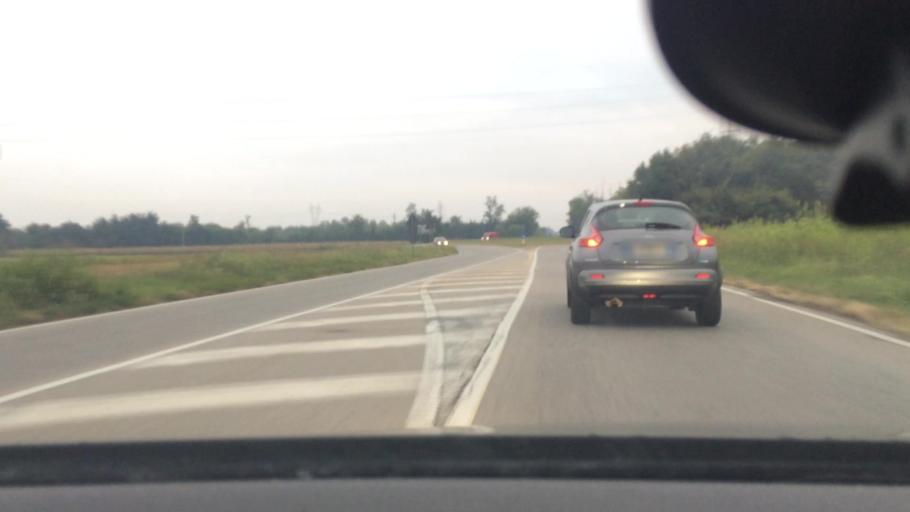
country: IT
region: Lombardy
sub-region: Citta metropolitana di Milano
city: Parabiago
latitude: 45.5415
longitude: 8.9591
